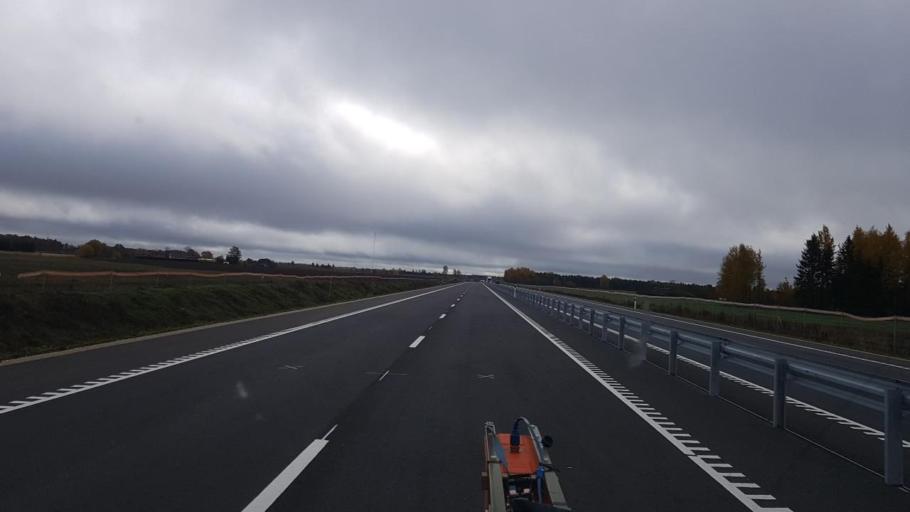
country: EE
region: Jaervamaa
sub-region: Paide linn
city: Paide
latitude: 59.0069
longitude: 25.5652
